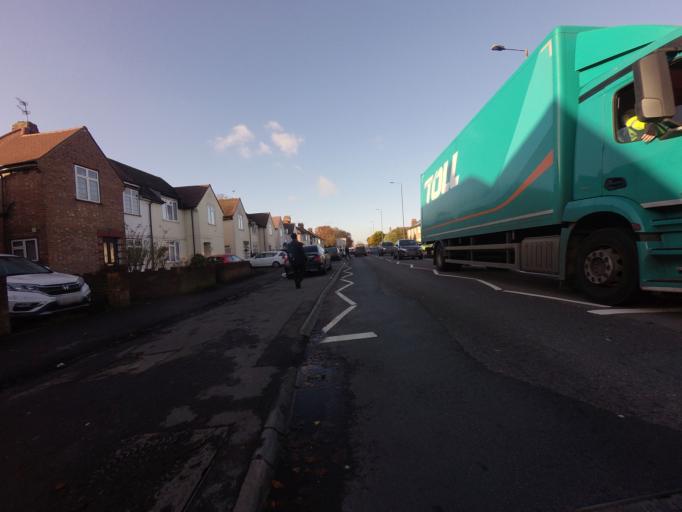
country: GB
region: England
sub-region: Greater London
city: Feltham
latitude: 51.4506
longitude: -0.4045
